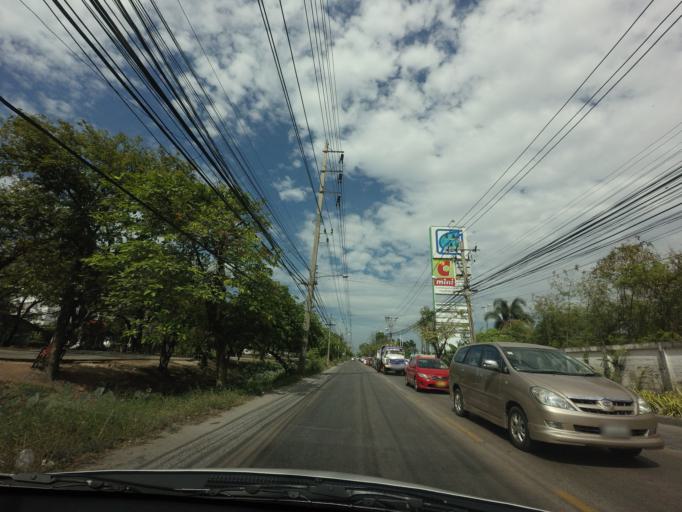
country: TH
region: Bangkok
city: Phra Khanong
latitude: 13.6664
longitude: 100.5918
